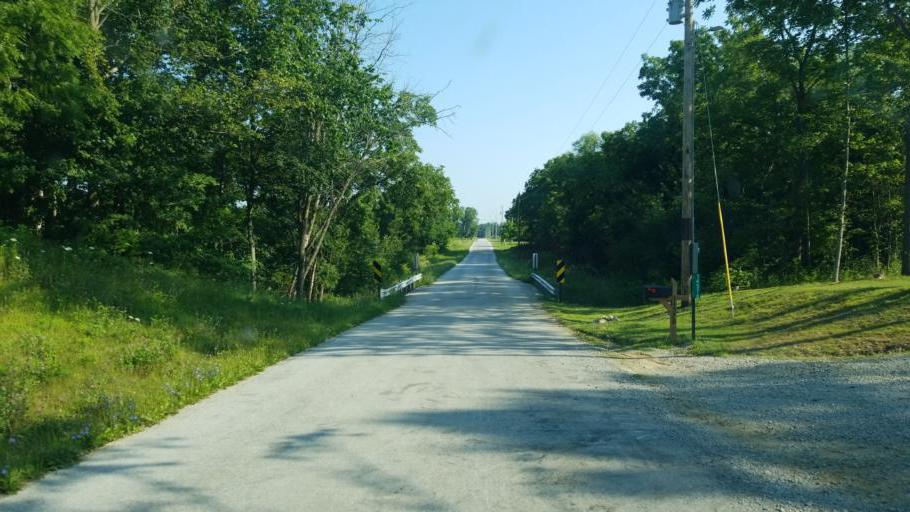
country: US
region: Ohio
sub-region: Hardin County
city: Kenton
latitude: 40.6069
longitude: -83.5410
